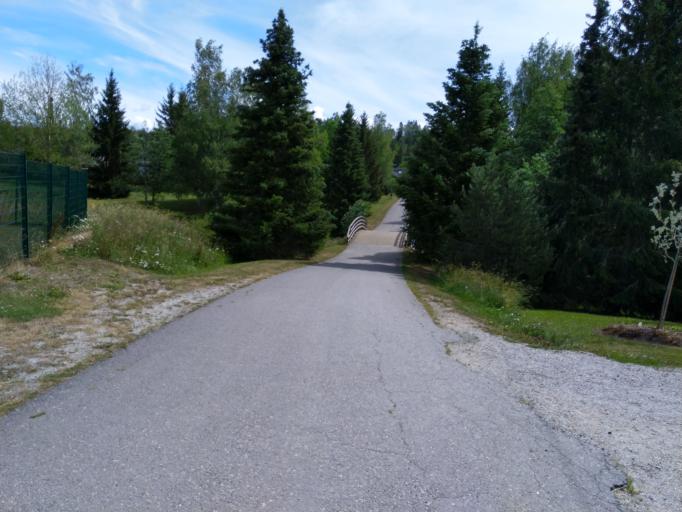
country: FI
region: Varsinais-Suomi
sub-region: Salo
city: Halikko
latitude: 60.4003
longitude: 23.0819
